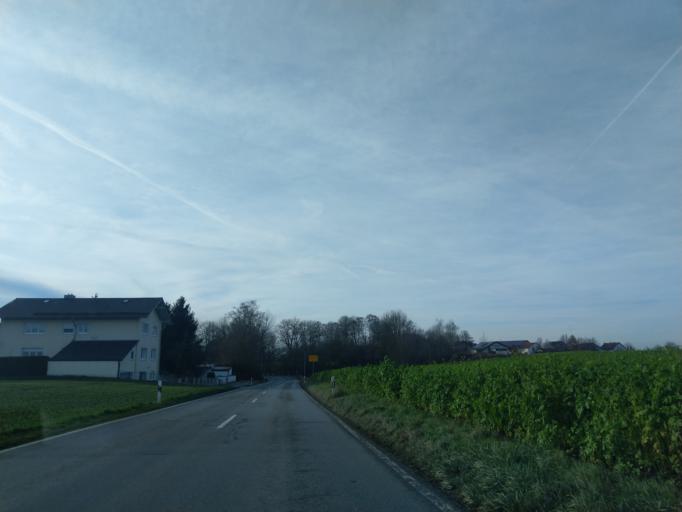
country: DE
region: Bavaria
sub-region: Lower Bavaria
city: Osterhofen
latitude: 48.7020
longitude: 12.9805
